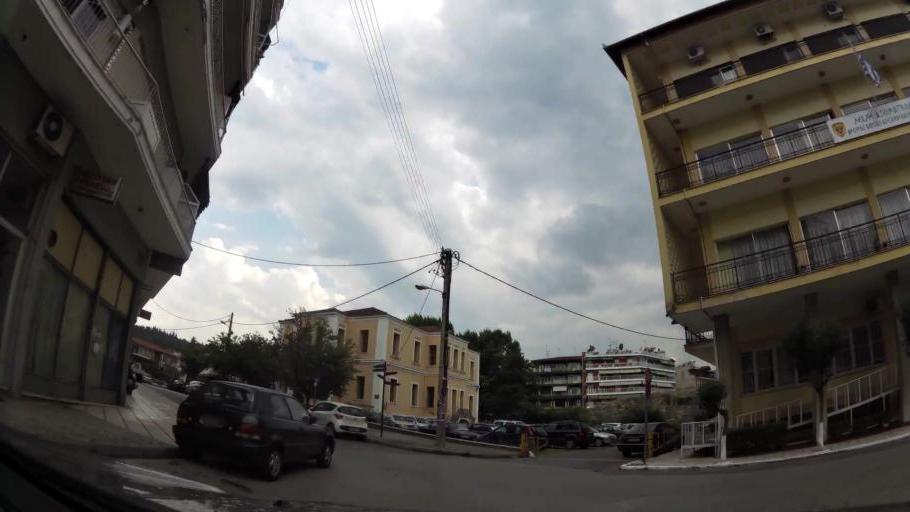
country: GR
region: Central Macedonia
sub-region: Nomos Imathias
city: Veroia
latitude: 40.5209
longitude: 22.2001
